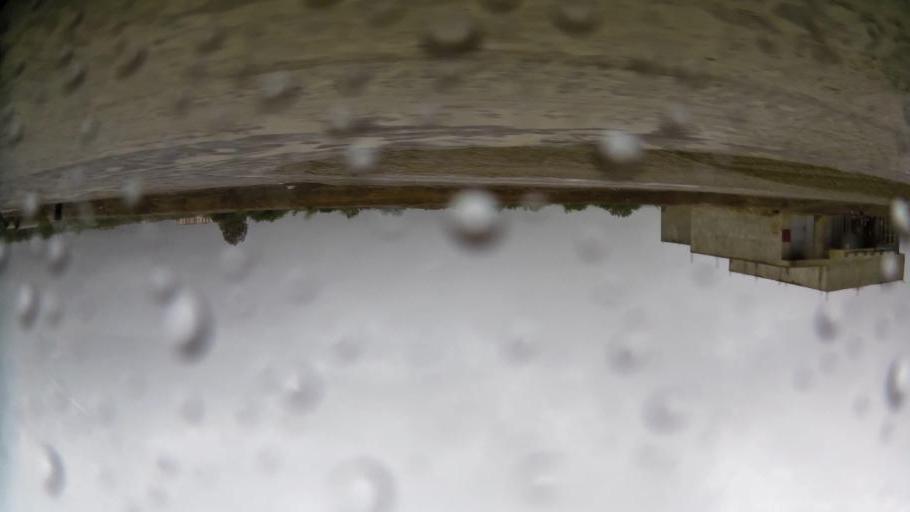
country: MA
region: Oriental
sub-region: Nador
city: Midar
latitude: 34.8740
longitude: -3.7259
